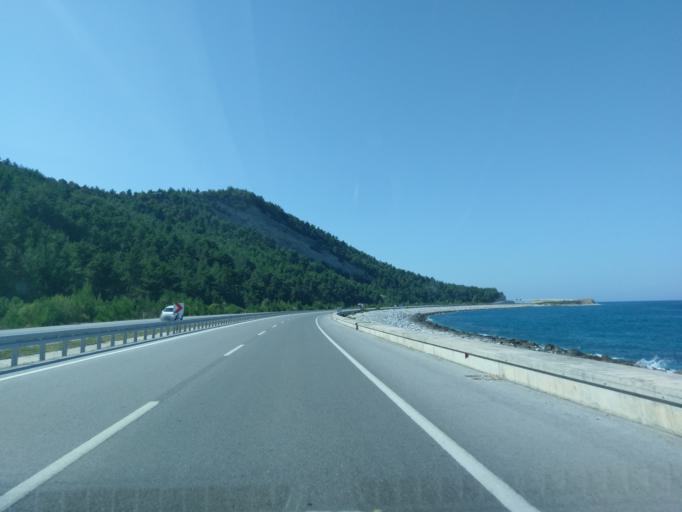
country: TR
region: Samsun
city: Yakakent
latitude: 41.6722
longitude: 35.4242
